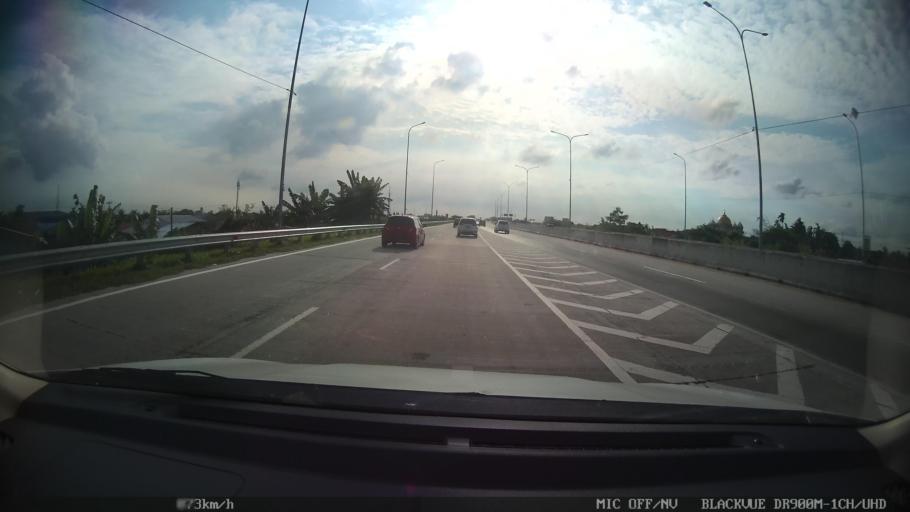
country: ID
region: North Sumatra
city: Medan
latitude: 3.6477
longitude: 98.6748
